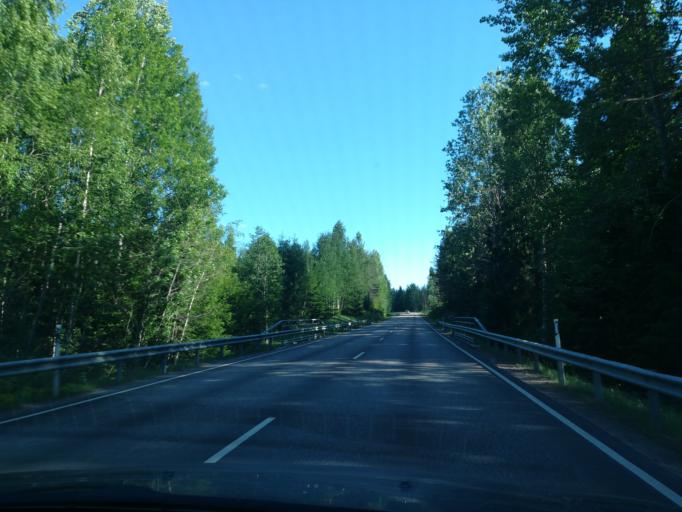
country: FI
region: South Karelia
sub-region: Imatra
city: Ruokolahti
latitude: 61.3798
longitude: 28.6555
